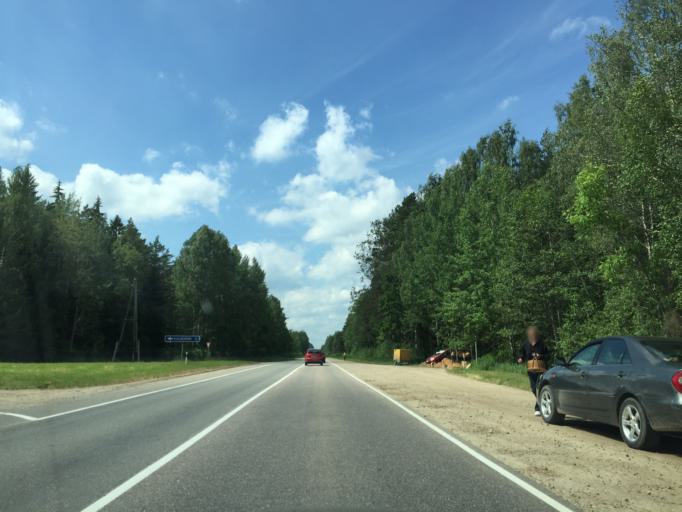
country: LV
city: Tireli
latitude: 56.9278
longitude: 23.5282
